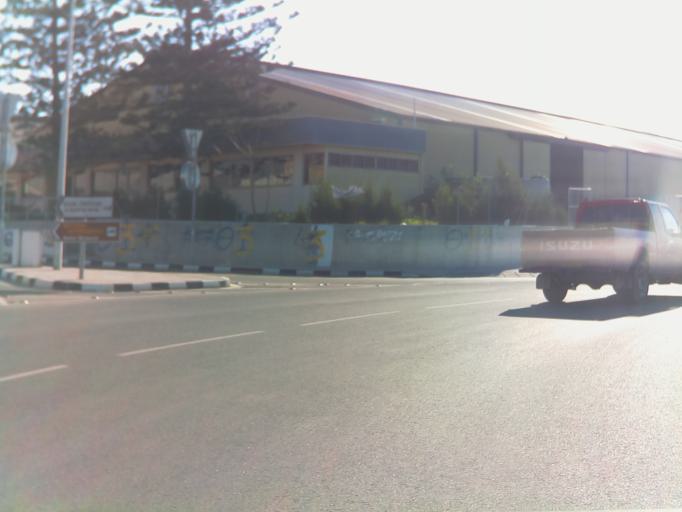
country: CY
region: Limassol
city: Ypsonas
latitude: 34.6654
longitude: 32.9913
